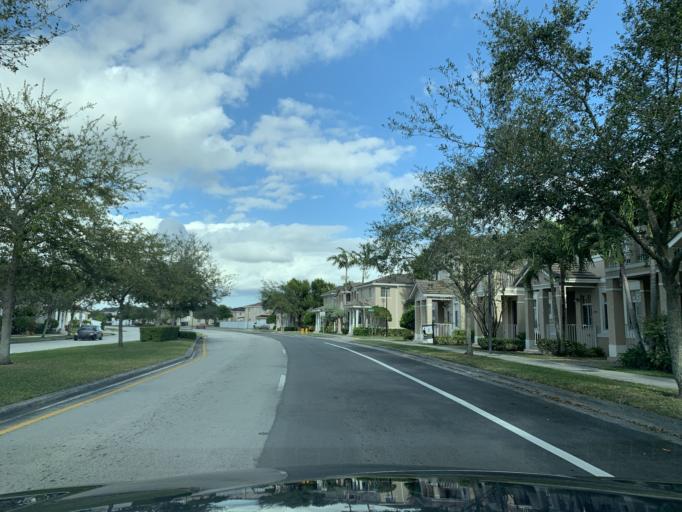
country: US
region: Florida
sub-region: Miami-Dade County
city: Naranja
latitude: 25.5079
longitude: -80.4195
